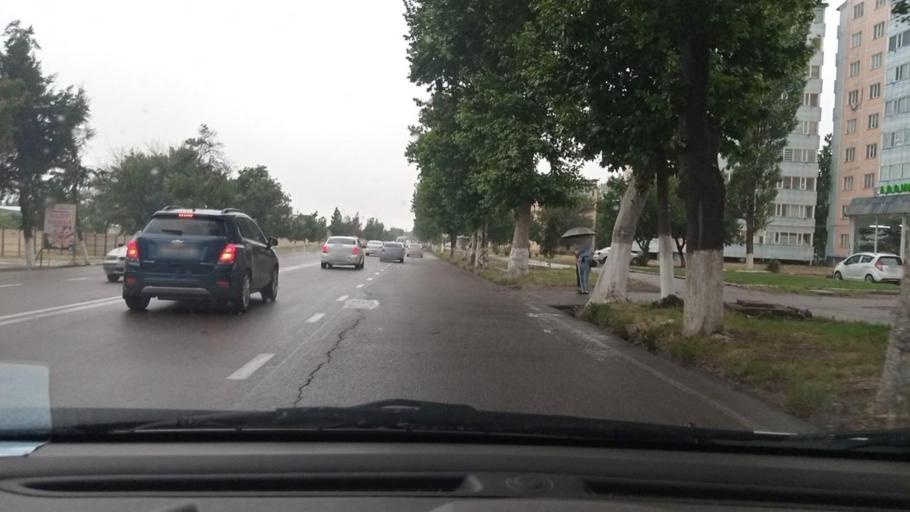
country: UZ
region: Toshkent
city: Angren
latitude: 41.0011
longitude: 70.0773
